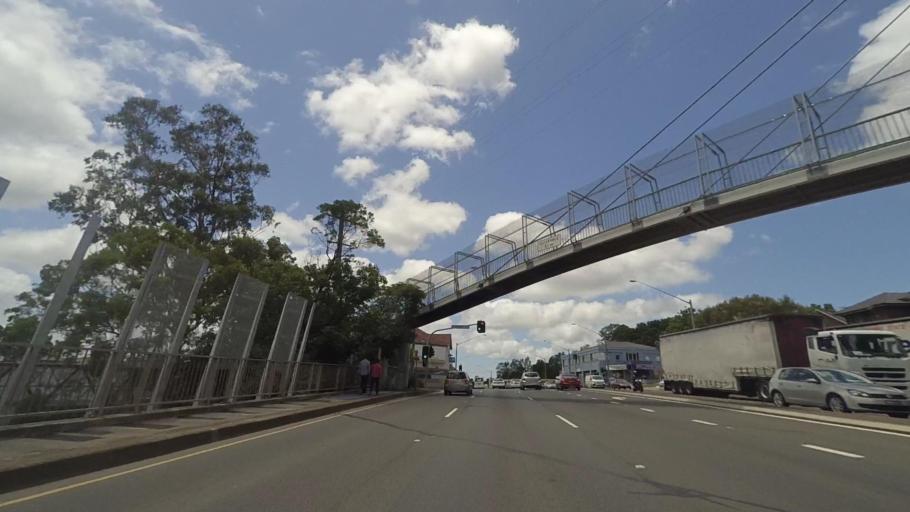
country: AU
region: New South Wales
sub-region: Hornsby Shire
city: Pennant Hills
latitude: -33.7390
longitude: 151.0715
